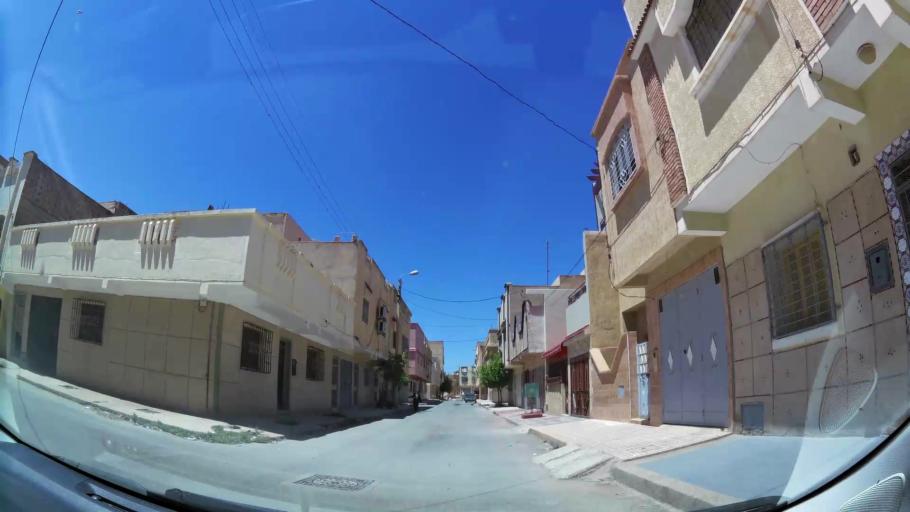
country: MA
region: Oriental
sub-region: Oujda-Angad
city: Oujda
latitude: 34.6824
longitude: -1.8741
